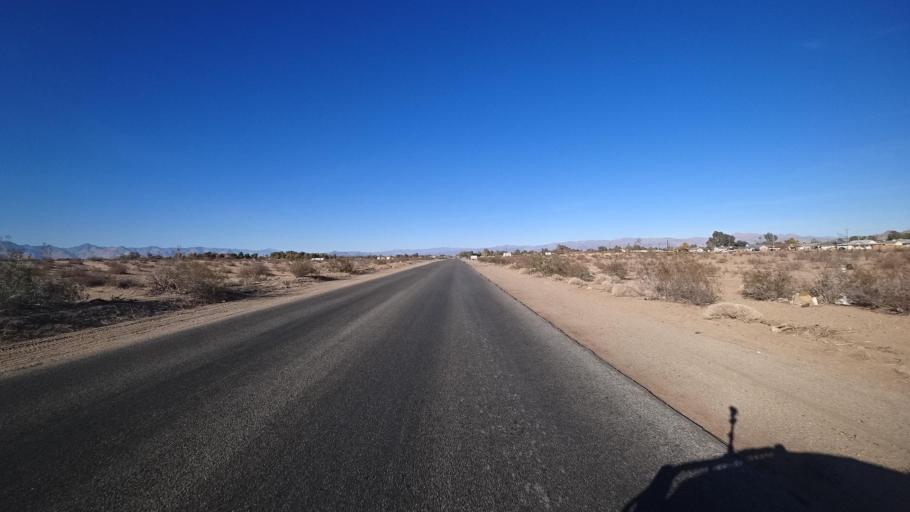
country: US
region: California
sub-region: Kern County
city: Ridgecrest
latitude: 35.6249
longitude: -117.6966
